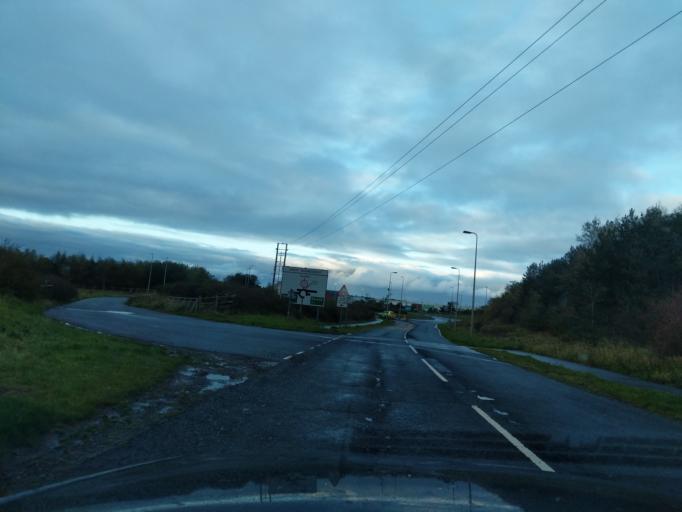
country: GB
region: Scotland
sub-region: East Lothian
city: Dunbar
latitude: 55.9866
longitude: -2.5143
